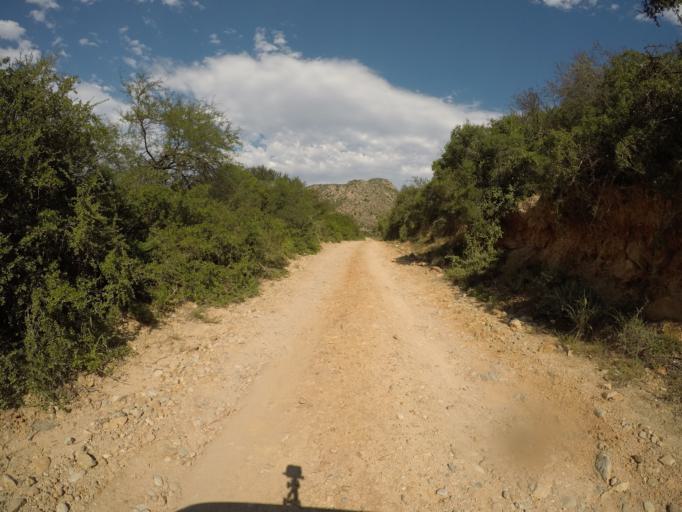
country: ZA
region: Eastern Cape
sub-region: Cacadu District Municipality
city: Kareedouw
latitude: -33.6534
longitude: 24.4185
